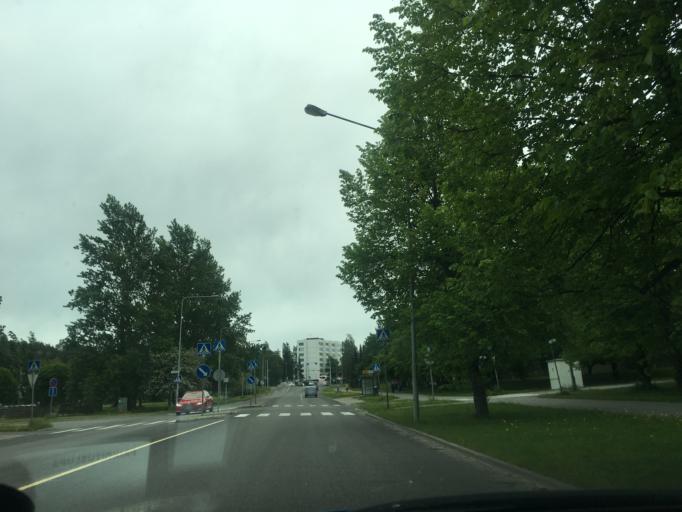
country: FI
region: Varsinais-Suomi
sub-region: Turku
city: Turku
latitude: 60.4604
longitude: 22.3066
